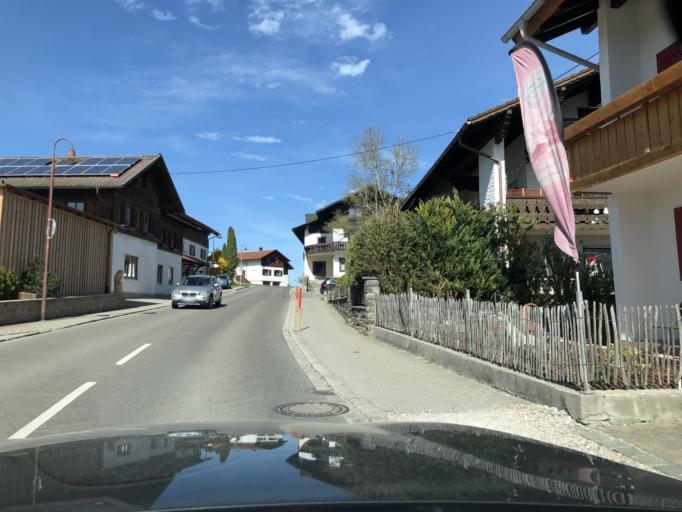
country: DE
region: Bavaria
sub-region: Swabia
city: Hopferau
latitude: 47.6126
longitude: 10.6336
